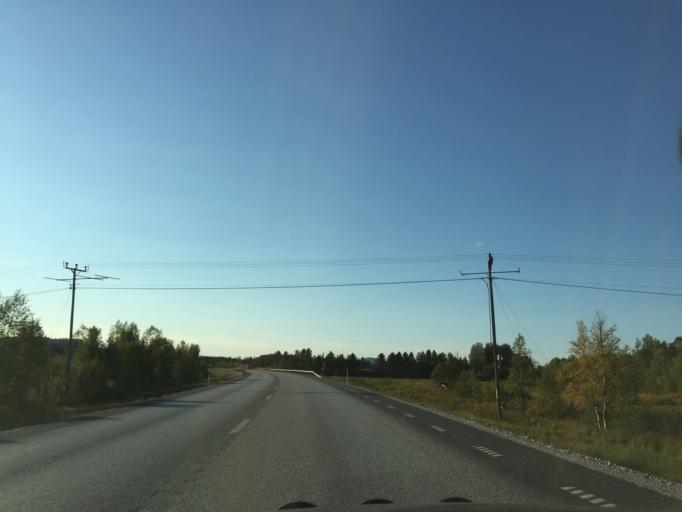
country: SE
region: Norrbotten
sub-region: Gallivare Kommun
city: Malmberget
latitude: 67.6436
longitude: 21.0512
